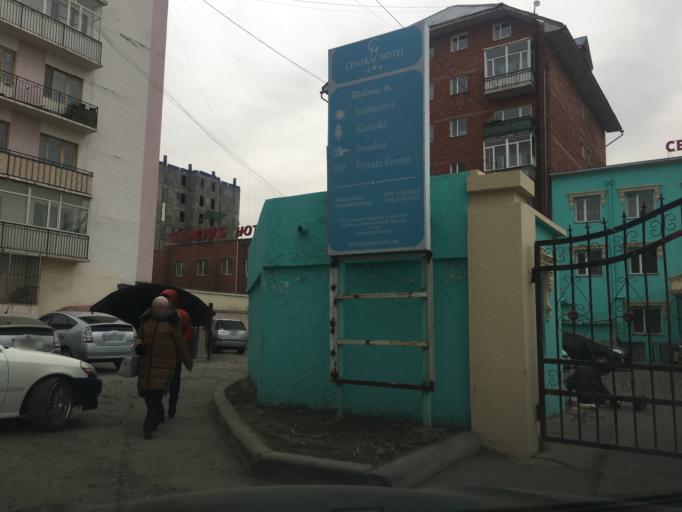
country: MN
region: Ulaanbaatar
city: Ulaanbaatar
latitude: 47.9105
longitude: 106.8849
